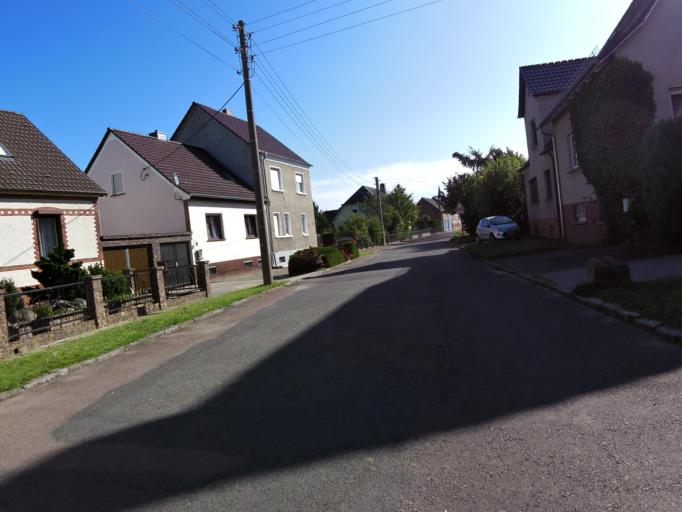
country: DE
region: Saxony-Anhalt
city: Rodleben
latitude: 51.8536
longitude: 12.1748
